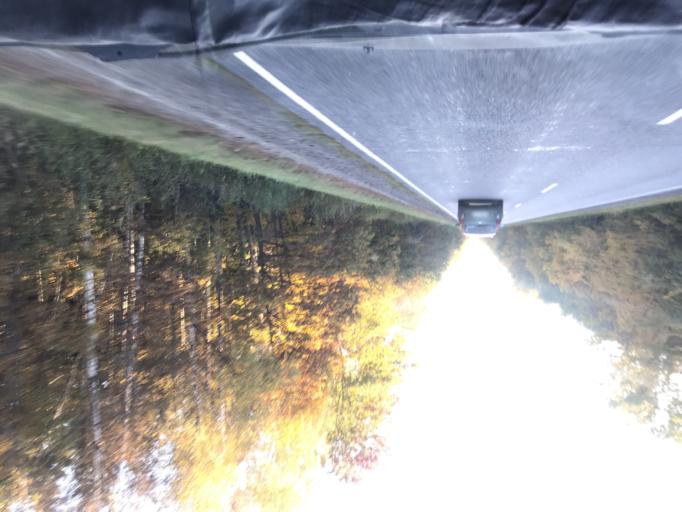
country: BY
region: Gomel
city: Zhytkavichy
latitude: 52.2733
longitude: 28.1059
